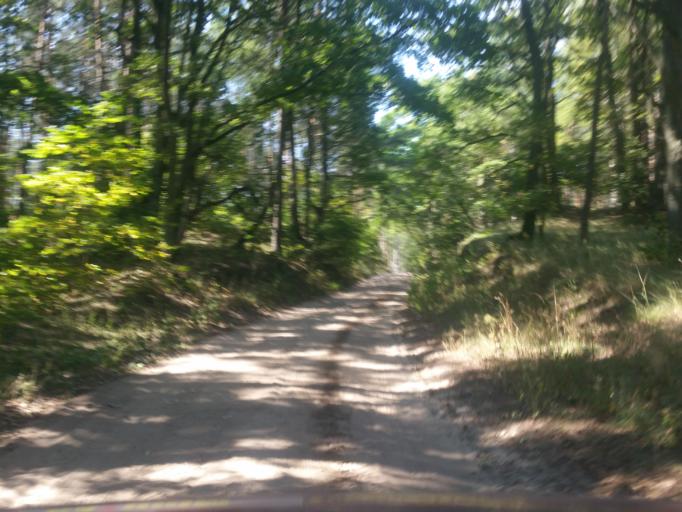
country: PL
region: Kujawsko-Pomorskie
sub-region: Powiat brodnicki
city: Brodnica
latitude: 53.2134
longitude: 19.3303
